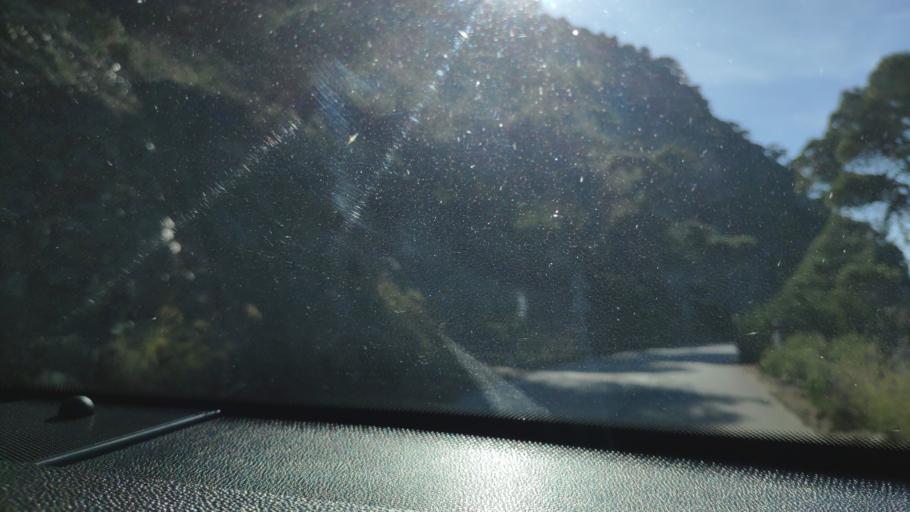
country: GR
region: Attica
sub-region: Nomarchia Dytikis Attikis
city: Kineta
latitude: 38.0642
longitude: 23.1300
